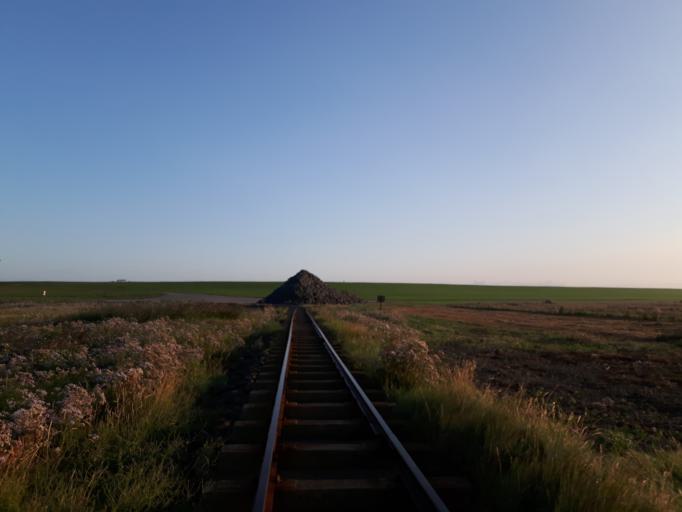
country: DE
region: Schleswig-Holstein
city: Dagebull
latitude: 54.7228
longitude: 8.7119
